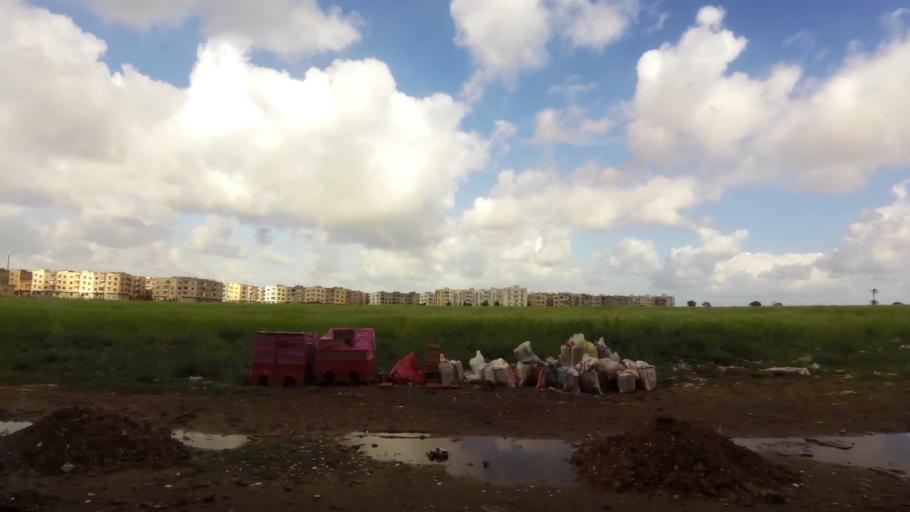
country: MA
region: Grand Casablanca
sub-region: Nouaceur
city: Bouskoura
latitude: 33.5345
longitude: -7.6988
